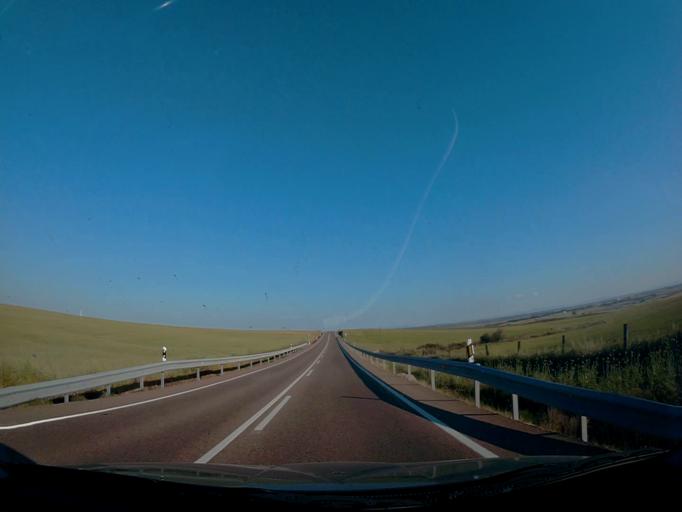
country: ES
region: Castille-La Mancha
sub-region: Province of Toledo
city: Maqueda
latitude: 40.0871
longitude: -4.3852
